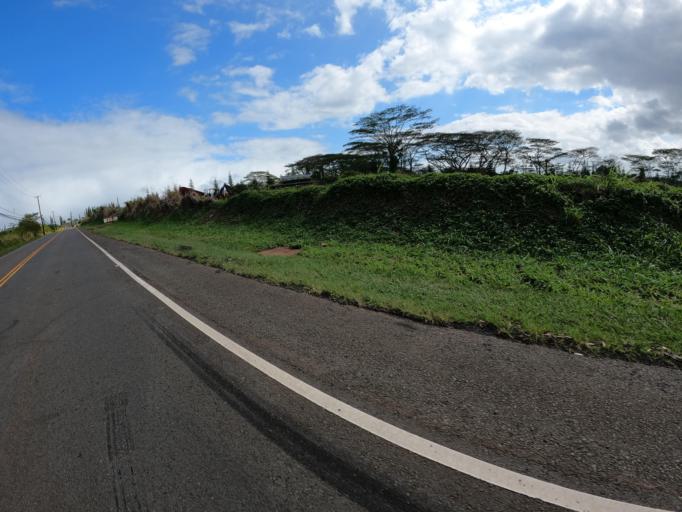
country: US
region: Hawaii
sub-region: Honolulu County
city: Whitmore Village
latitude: 21.5136
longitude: -158.0110
